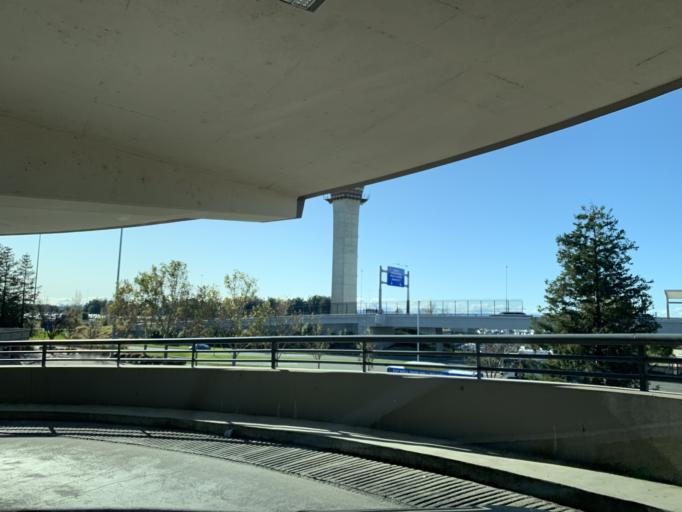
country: US
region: California
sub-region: Yolo County
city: West Sacramento
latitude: 38.6913
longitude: -121.5896
